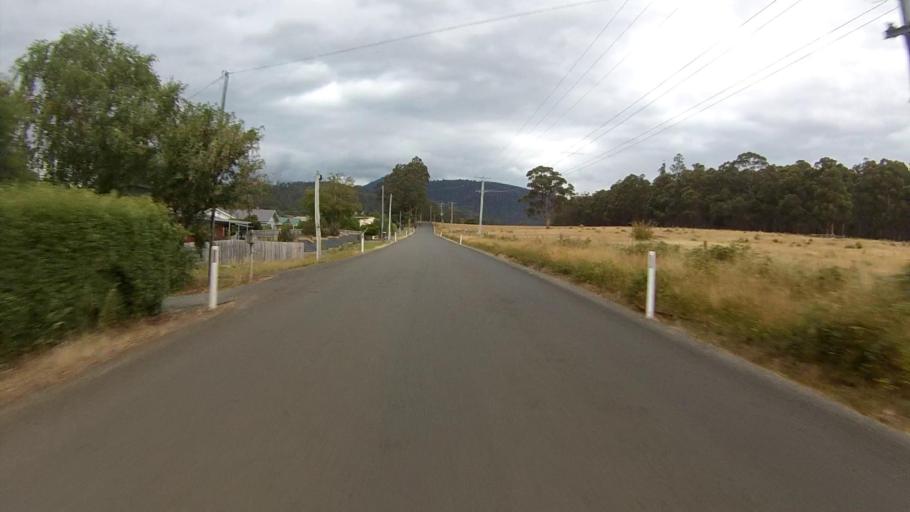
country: AU
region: Tasmania
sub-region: Huon Valley
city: Huonville
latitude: -42.9724
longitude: 147.0898
